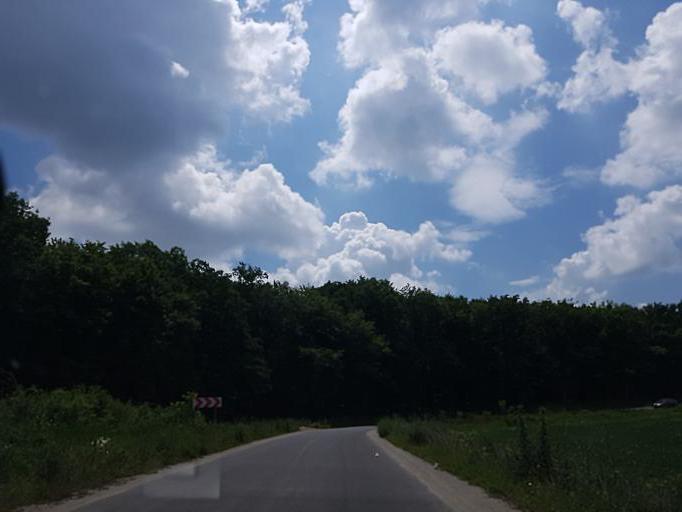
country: RO
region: Sibiu
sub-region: Comuna Seica Mica
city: Seica Mica
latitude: 46.0451
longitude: 24.1578
